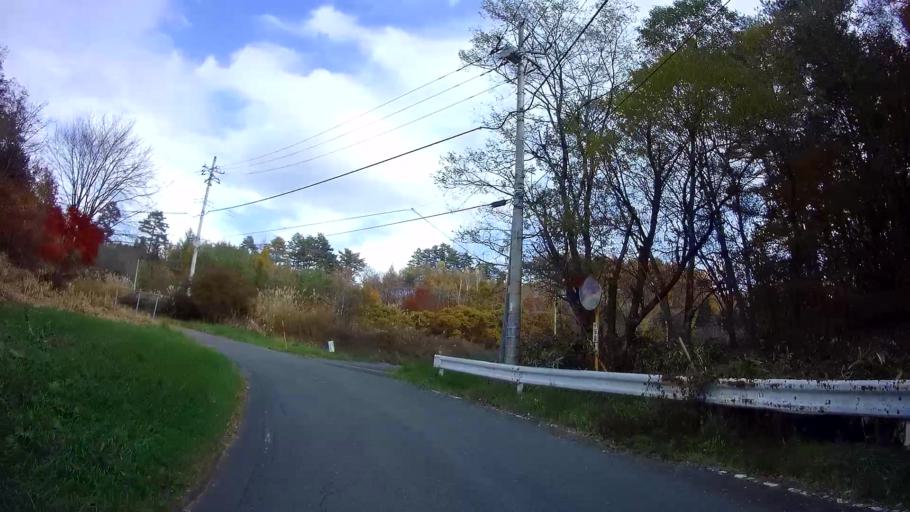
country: JP
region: Gunma
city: Nakanojomachi
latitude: 36.6353
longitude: 138.6400
